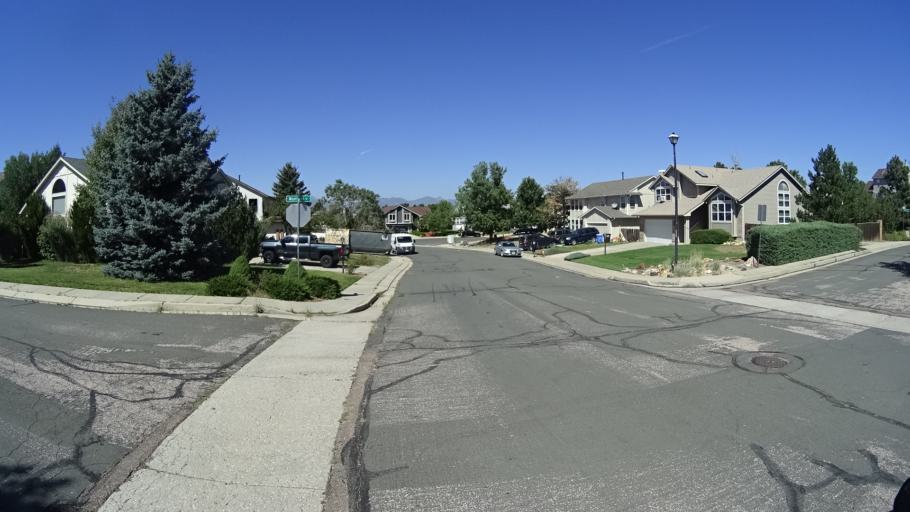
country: US
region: Colorado
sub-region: El Paso County
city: Black Forest
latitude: 38.9463
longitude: -104.7515
